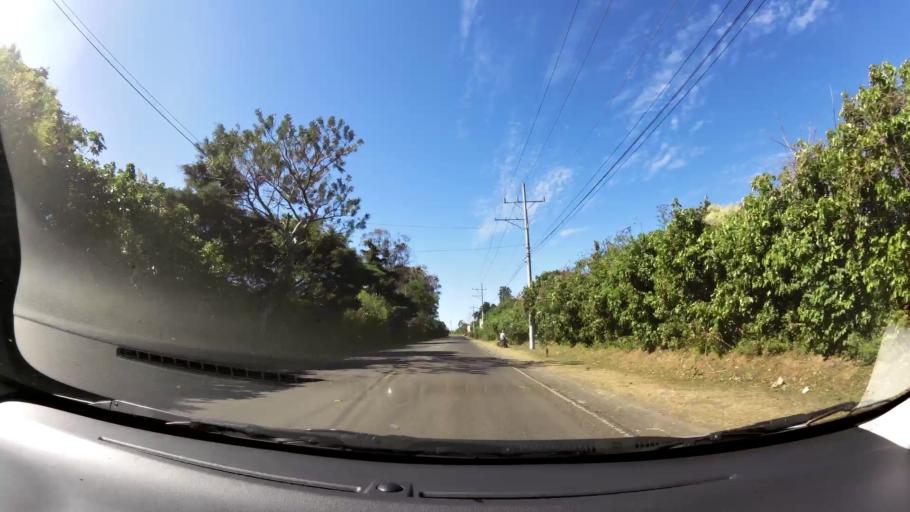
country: SV
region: Ahuachapan
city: Concepcion de Ataco
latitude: 13.8638
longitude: -89.8026
